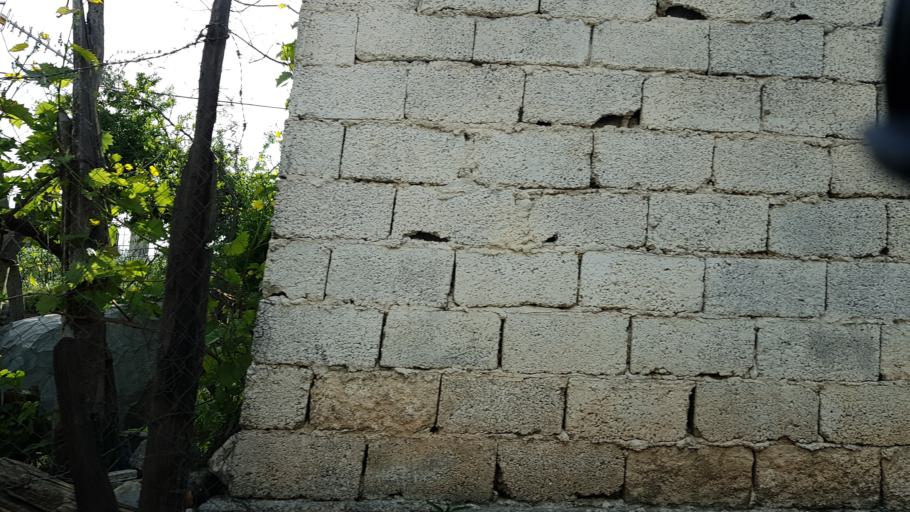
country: AL
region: Shkoder
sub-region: Rrethi i Shkodres
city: Shkoder
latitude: 42.0618
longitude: 19.5281
